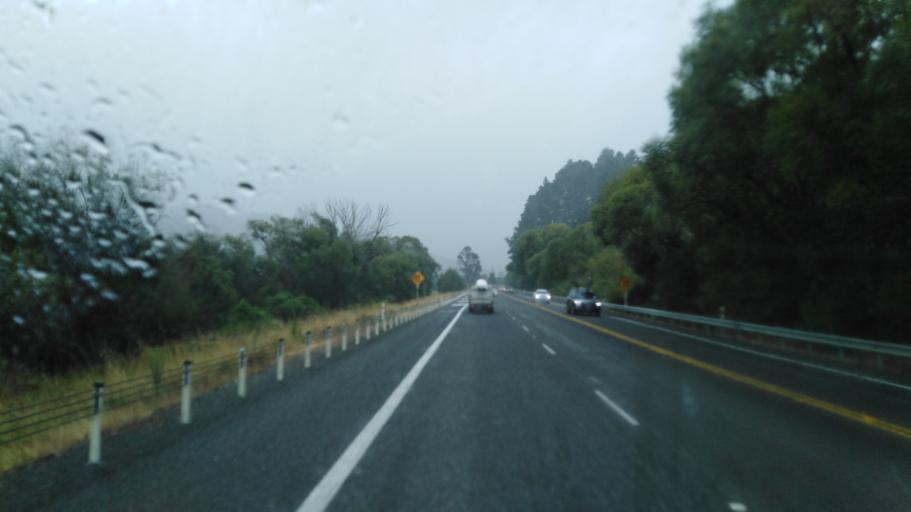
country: NZ
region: Marlborough
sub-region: Marlborough District
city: Picton
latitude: -41.3782
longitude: 173.9468
